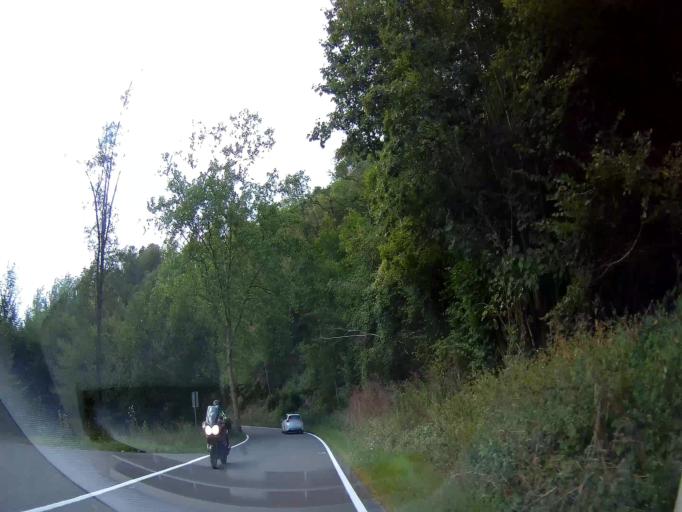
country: BE
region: Wallonia
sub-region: Province de Namur
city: Onhaye
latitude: 50.2985
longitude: 4.8152
